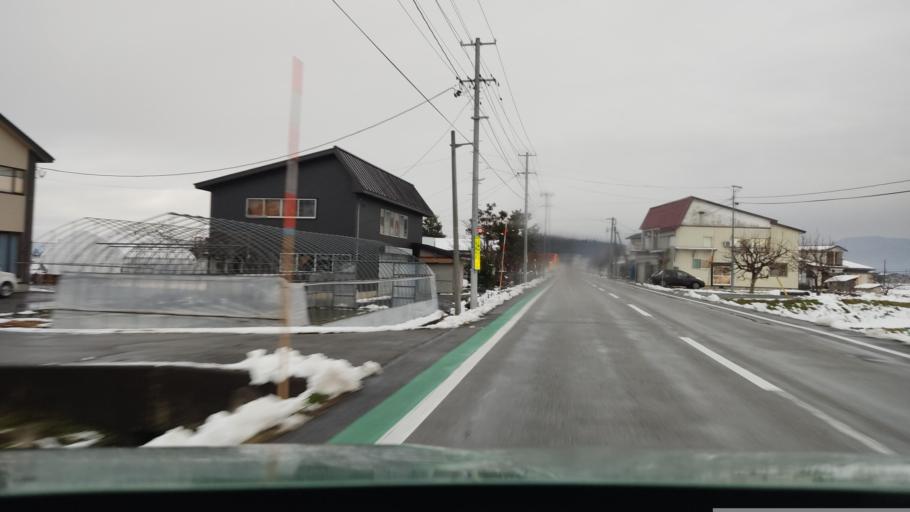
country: JP
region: Akita
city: Omagari
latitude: 39.4611
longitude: 140.5344
